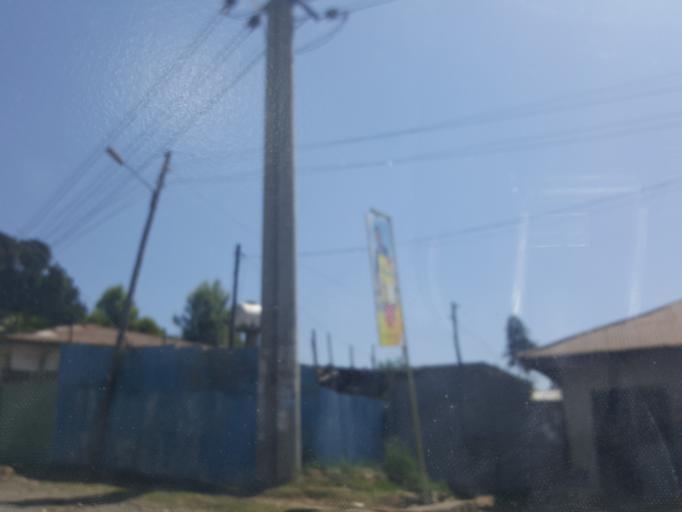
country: ET
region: Adis Abeba
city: Addis Ababa
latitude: 9.0527
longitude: 38.7395
